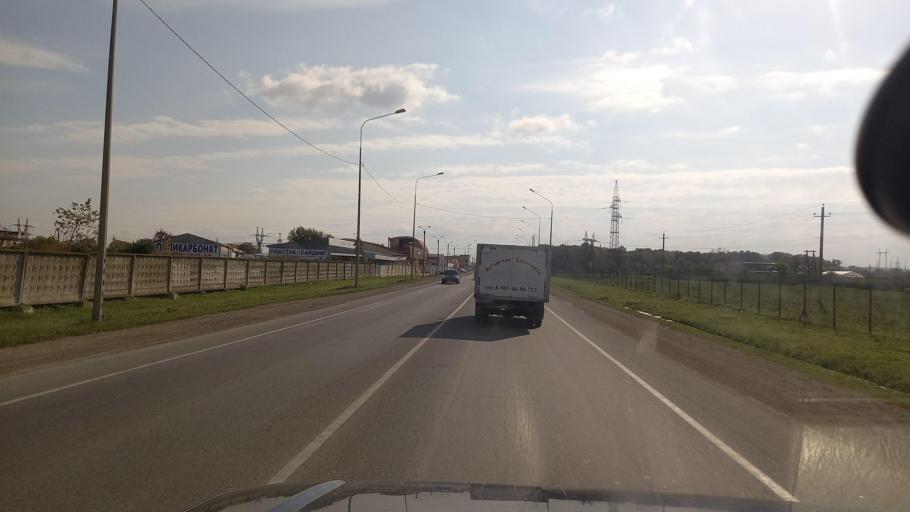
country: RU
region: Krasnodarskiy
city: Krymsk
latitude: 44.9110
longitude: 38.0186
